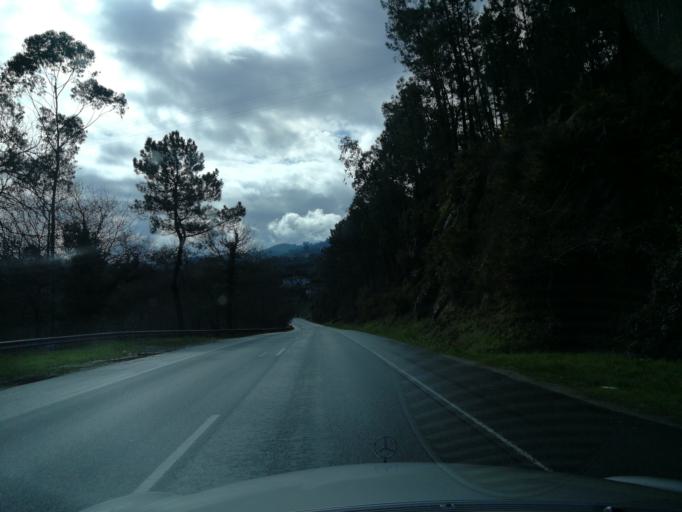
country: PT
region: Viana do Castelo
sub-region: Ponte da Barca
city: Ponte da Barca
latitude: 41.8083
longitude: -8.3728
